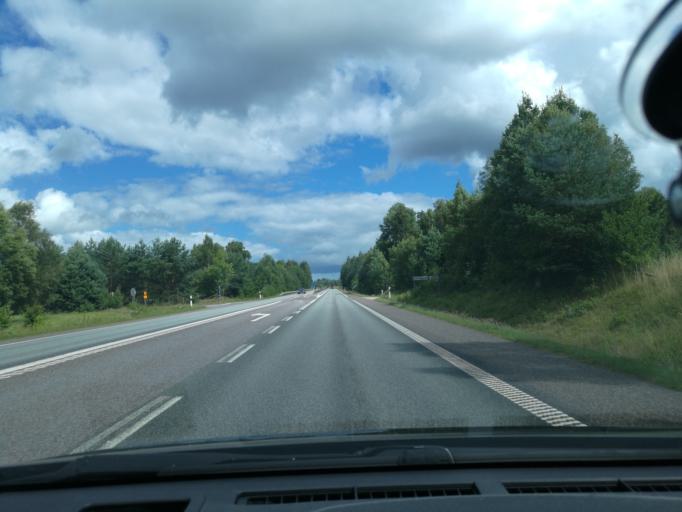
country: SE
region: Skane
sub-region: Hassleholms Kommun
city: Hastveda
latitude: 56.2482
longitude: 13.9201
